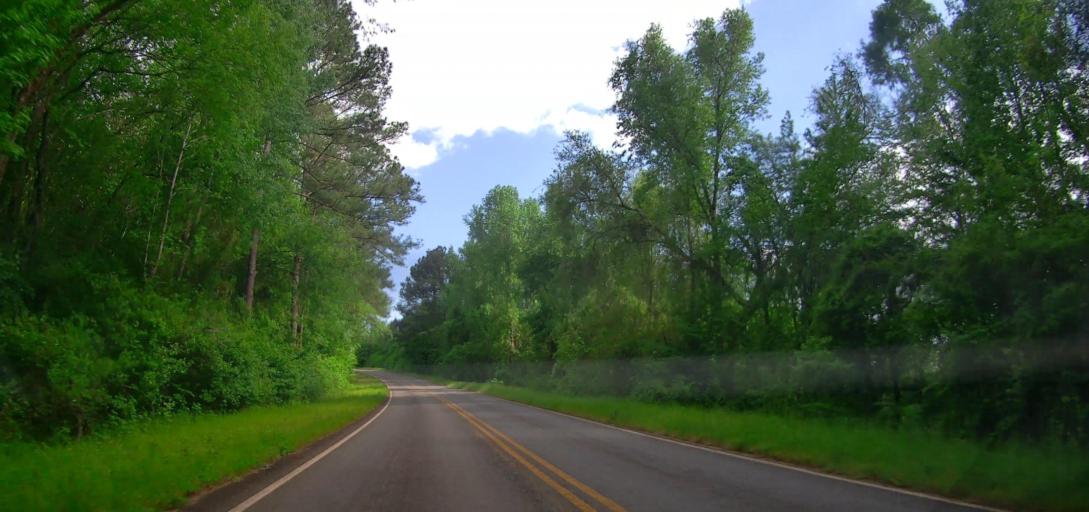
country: US
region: Georgia
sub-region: Laurens County
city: East Dublin
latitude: 32.7412
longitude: -82.9208
